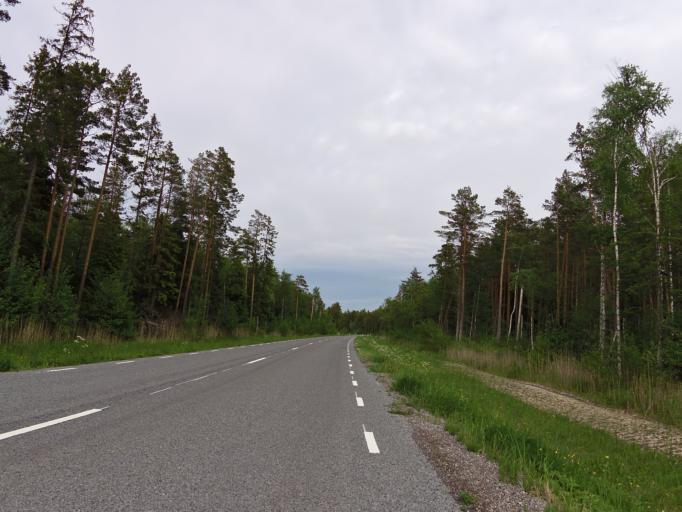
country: EE
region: Laeaene
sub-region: Ridala Parish
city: Uuemoisa
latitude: 59.2119
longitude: 23.7335
